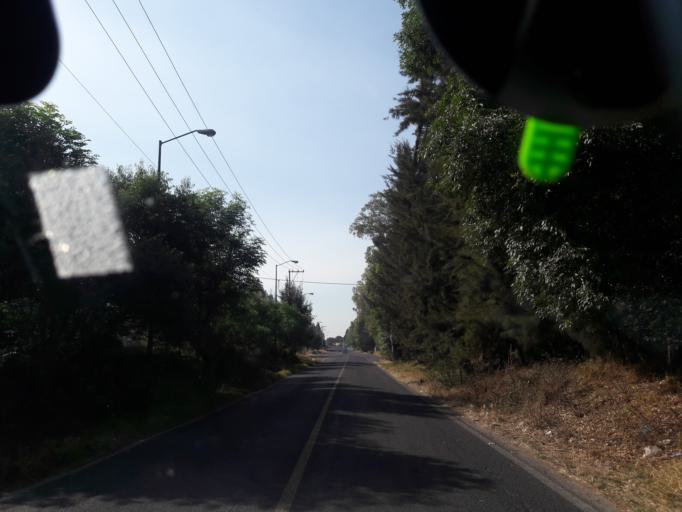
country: MX
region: Tlaxcala
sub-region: Ixtacuixtla de Mariano Matamoros
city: Villa Mariano Matamoros
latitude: 19.3130
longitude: -98.3865
